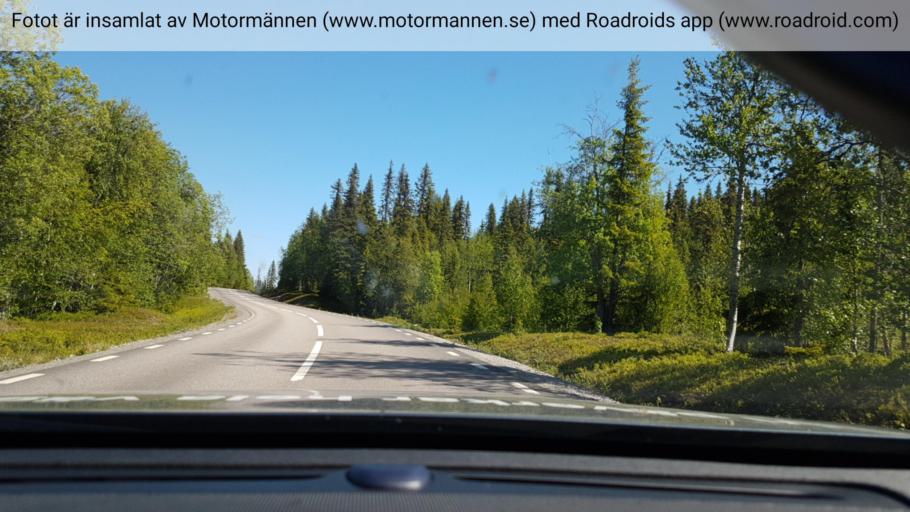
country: SE
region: Vaesterbotten
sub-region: Asele Kommun
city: Insjon
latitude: 64.7312
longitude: 17.5293
